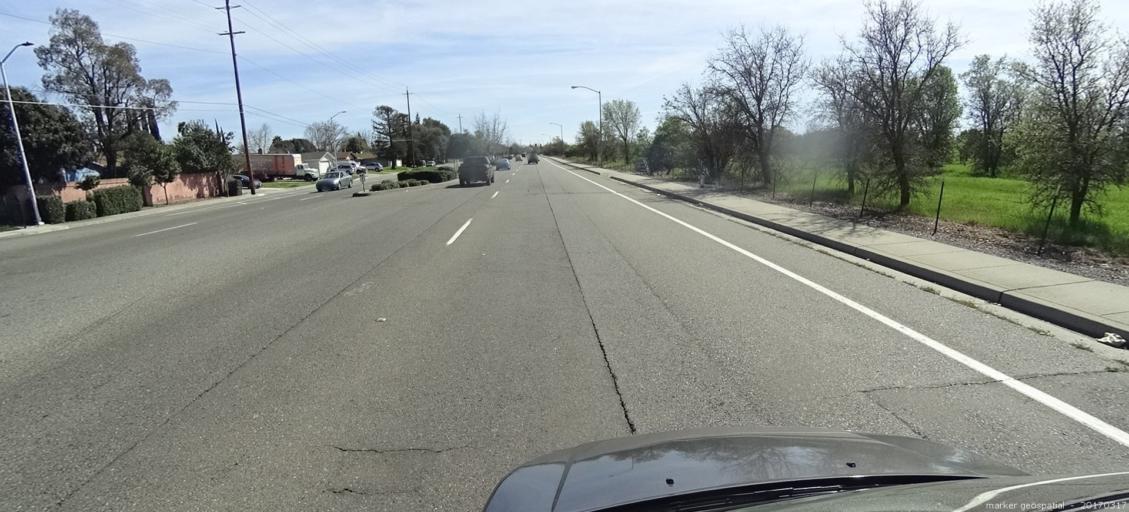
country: US
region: California
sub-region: Sacramento County
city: Laguna
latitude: 38.4557
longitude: -121.4458
